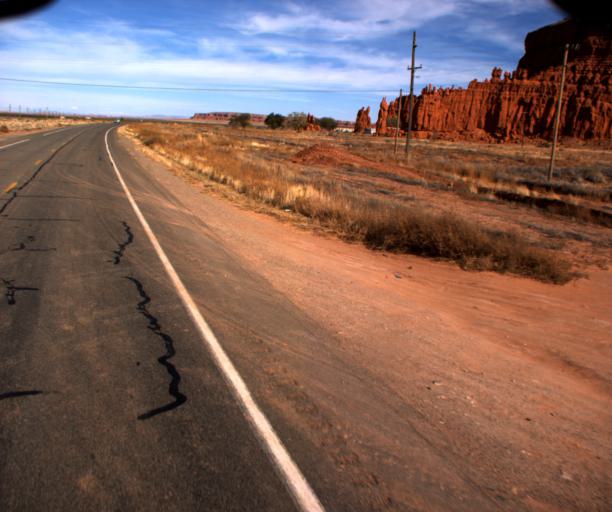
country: US
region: Arizona
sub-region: Navajo County
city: Kayenta
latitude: 36.7757
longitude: -110.0154
